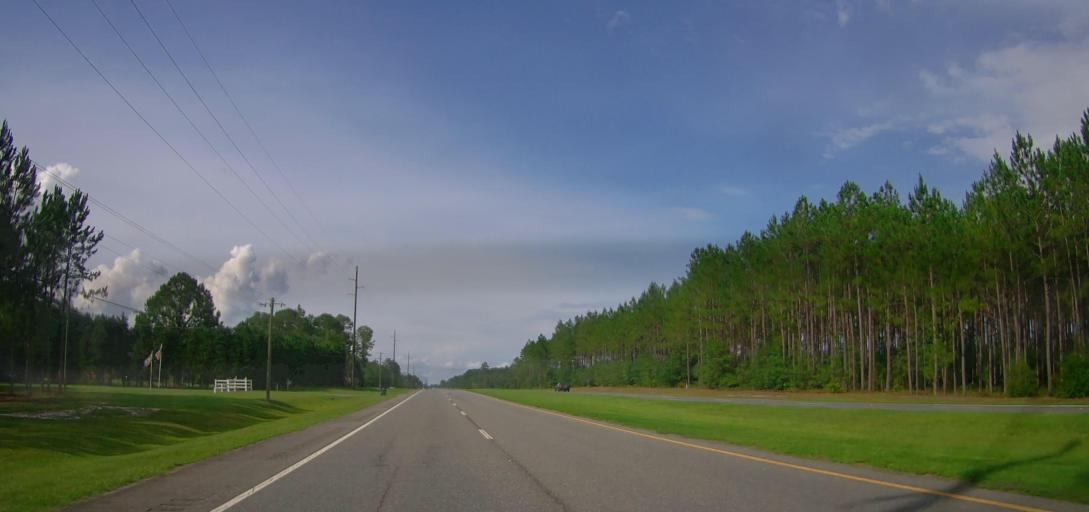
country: US
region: Georgia
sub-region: Wayne County
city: Jesup
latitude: 31.5152
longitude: -81.9937
